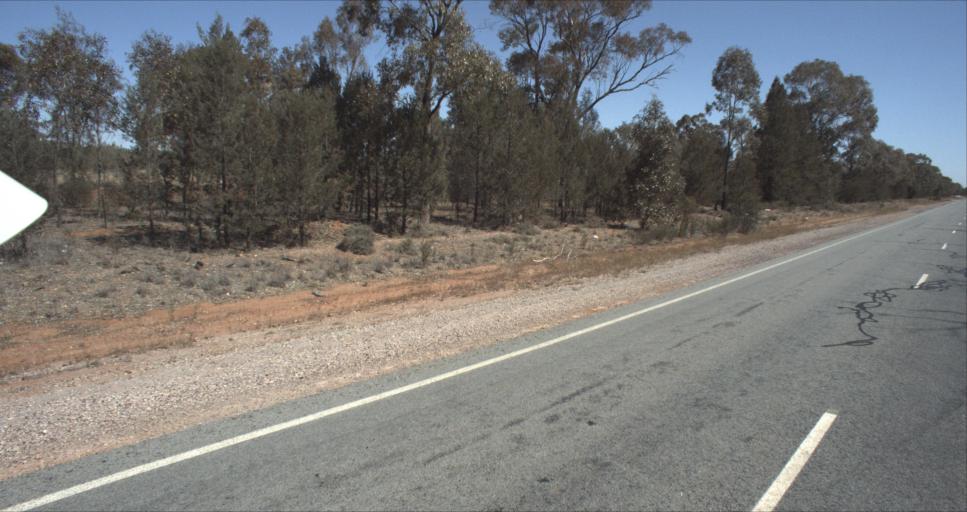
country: AU
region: New South Wales
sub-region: Leeton
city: Leeton
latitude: -34.4959
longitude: 146.4564
